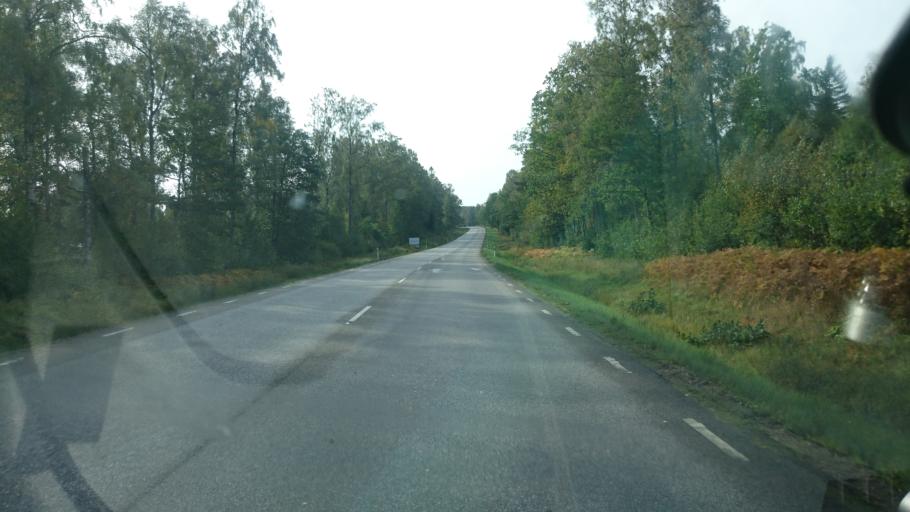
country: SE
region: Vaestra Goetaland
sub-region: Alingsas Kommun
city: Sollebrunn
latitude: 58.0800
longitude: 12.4866
